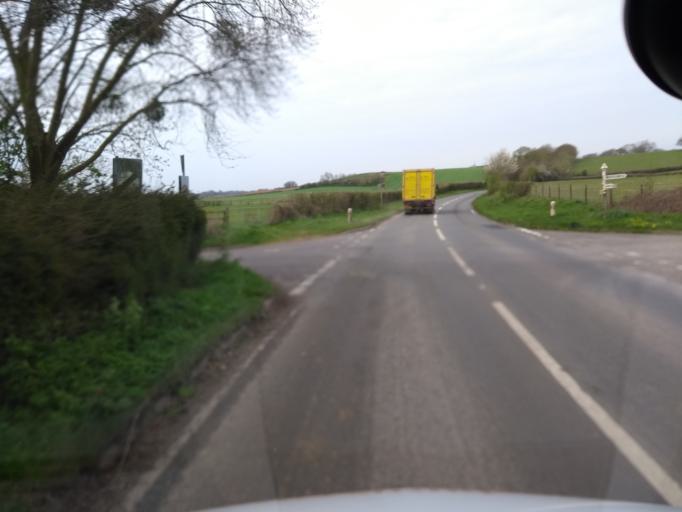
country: GB
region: England
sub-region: Somerset
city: Creech Saint Michael
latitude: 50.9979
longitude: -2.9987
